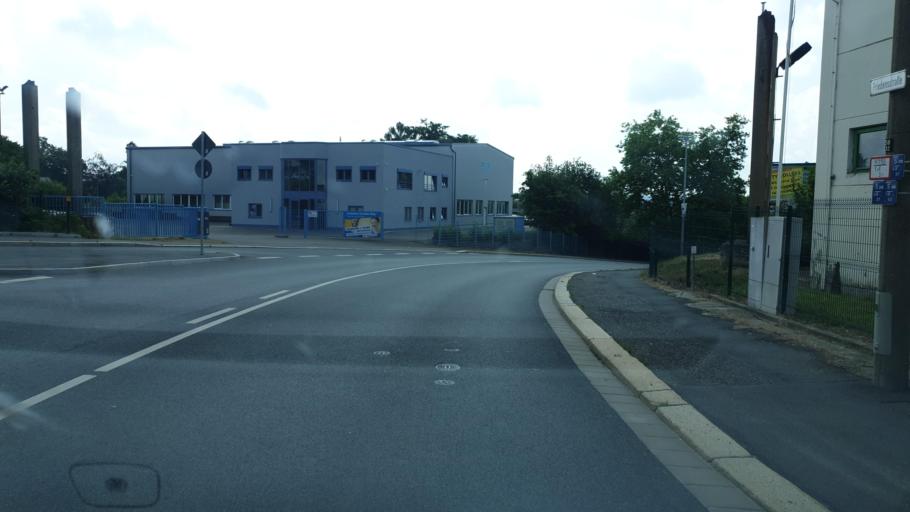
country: DE
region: Saxony
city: Reichenbach/Vogtland
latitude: 50.6283
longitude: 12.3011
